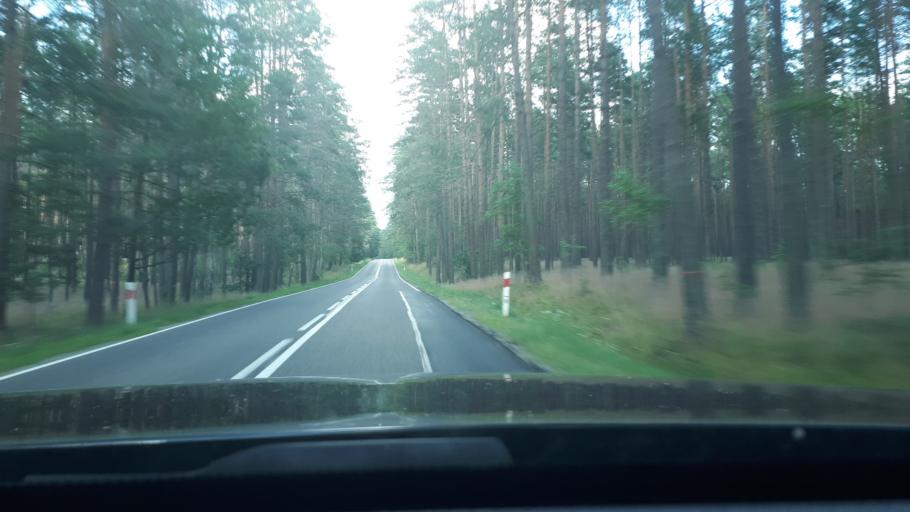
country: PL
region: Warmian-Masurian Voivodeship
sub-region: Powiat olsztynski
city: Stawiguda
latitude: 53.5379
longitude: 20.5282
